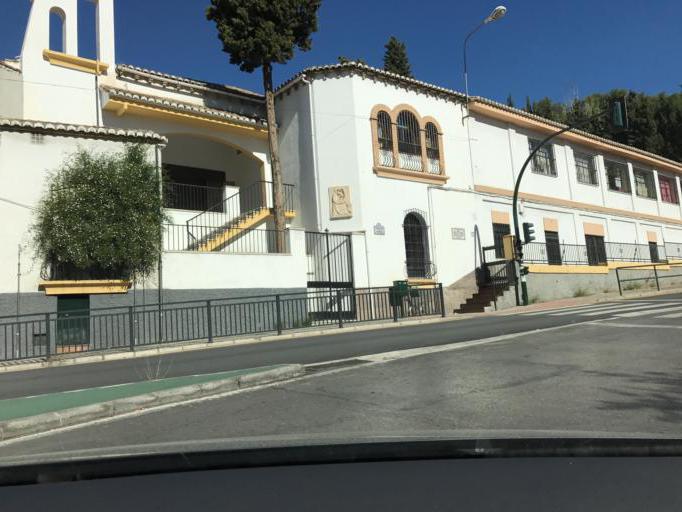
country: ES
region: Andalusia
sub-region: Provincia de Granada
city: Granada
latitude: 37.1880
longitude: -3.6000
